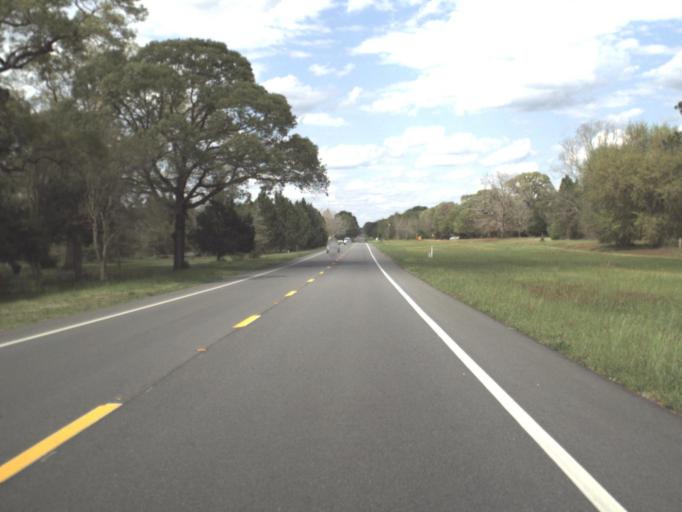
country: US
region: Florida
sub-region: Okaloosa County
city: Crestview
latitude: 30.9061
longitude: -86.4896
